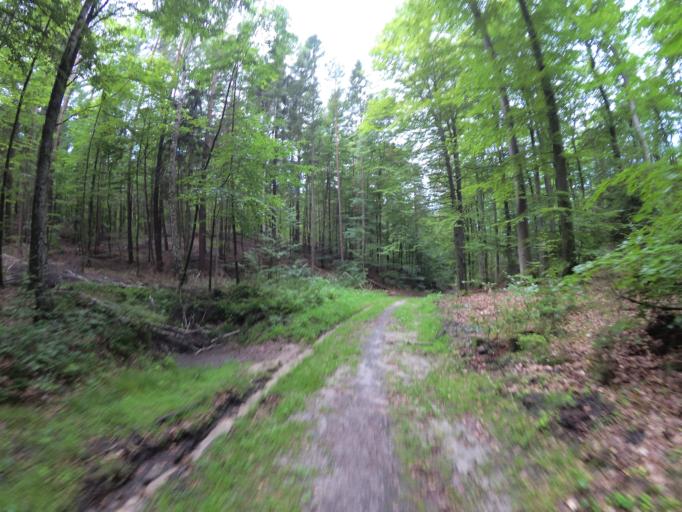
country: PL
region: Pomeranian Voivodeship
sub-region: Gdynia
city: Wielki Kack
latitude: 54.5054
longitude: 18.4468
